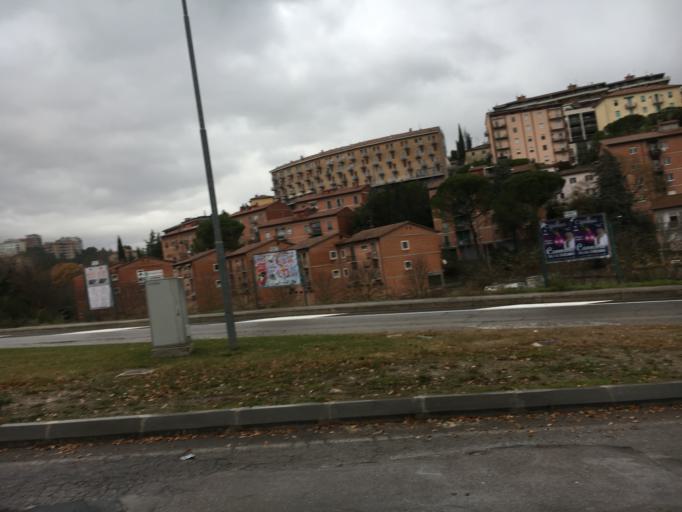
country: IT
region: Umbria
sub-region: Provincia di Perugia
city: Perugia
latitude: 43.1177
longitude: 12.3724
